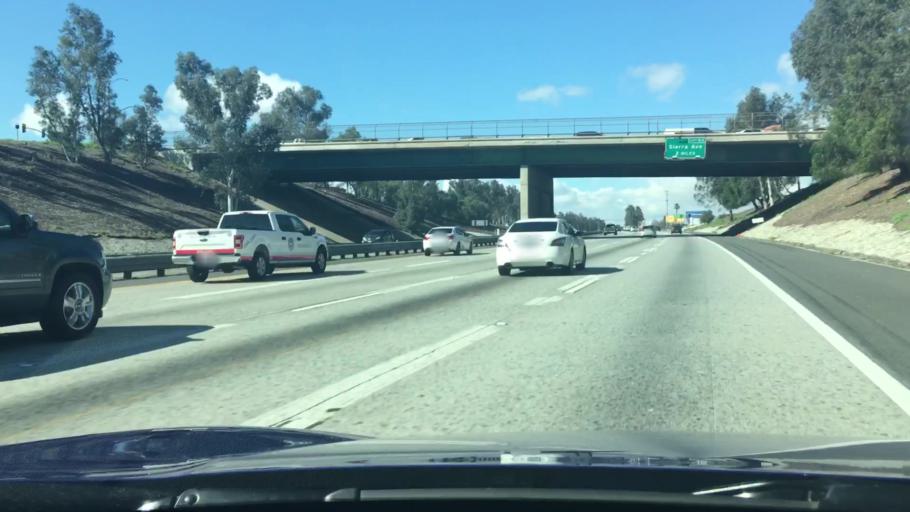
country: US
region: California
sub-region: San Bernardino County
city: Bloomington
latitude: 34.0686
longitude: -117.3951
